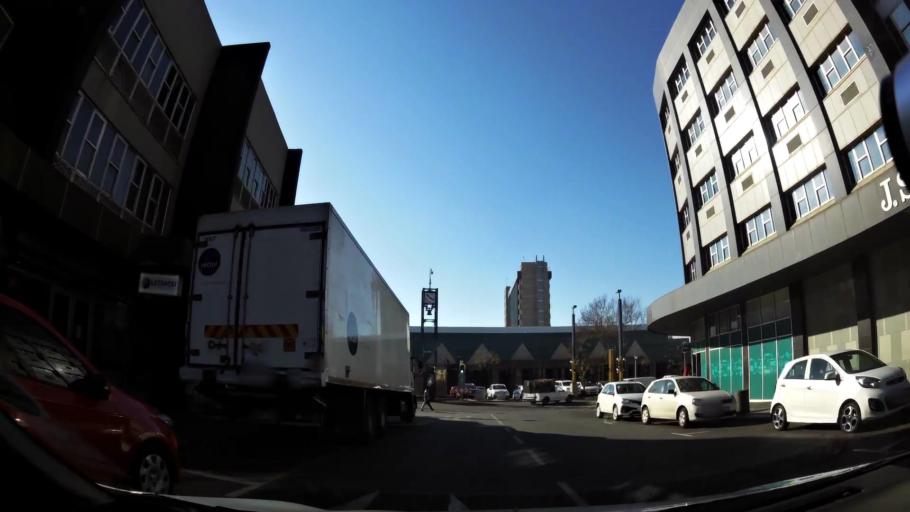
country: ZA
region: Gauteng
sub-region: Ekurhuleni Metropolitan Municipality
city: Germiston
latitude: -26.2647
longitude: 28.1213
